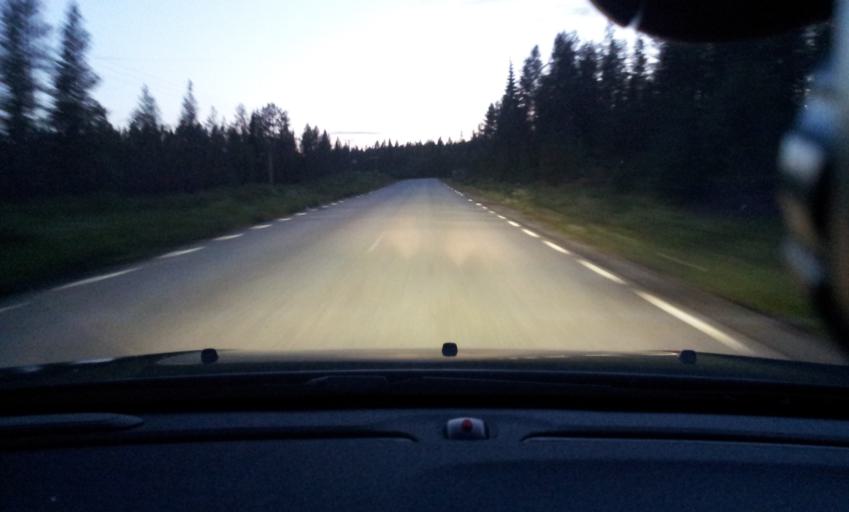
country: SE
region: Jaemtland
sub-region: Bergs Kommun
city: Hoverberg
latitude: 62.6790
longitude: 14.6661
